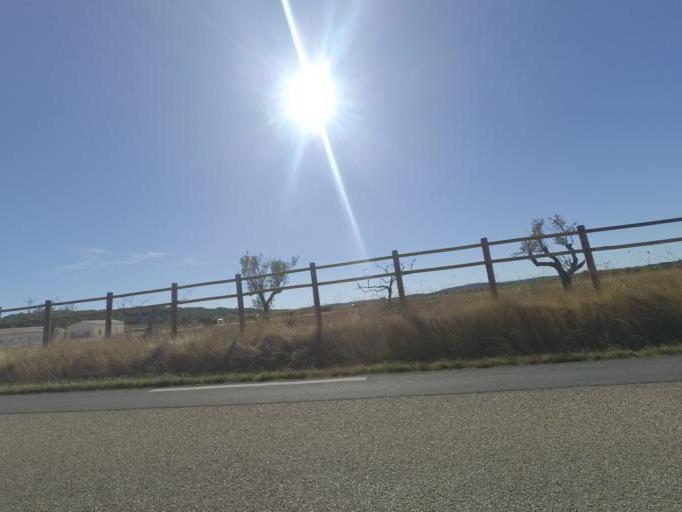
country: FR
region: Languedoc-Roussillon
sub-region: Departement du Gard
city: Nages-et-Solorgues
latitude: 43.7778
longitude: 4.2233
